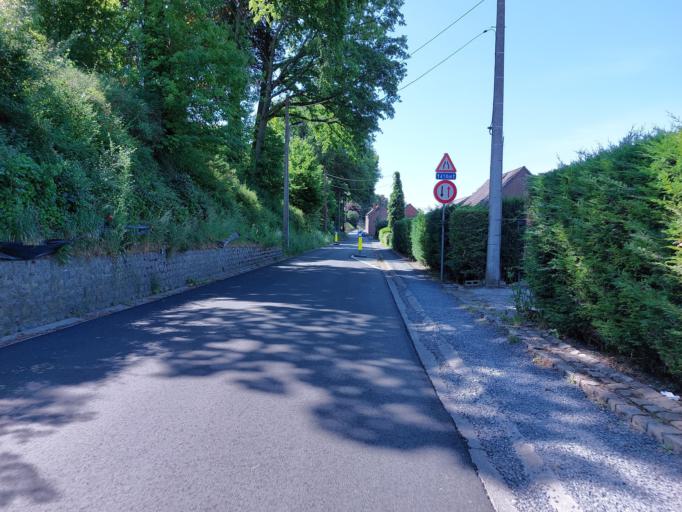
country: BE
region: Wallonia
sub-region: Province du Hainaut
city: Mons
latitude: 50.4421
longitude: 3.9701
